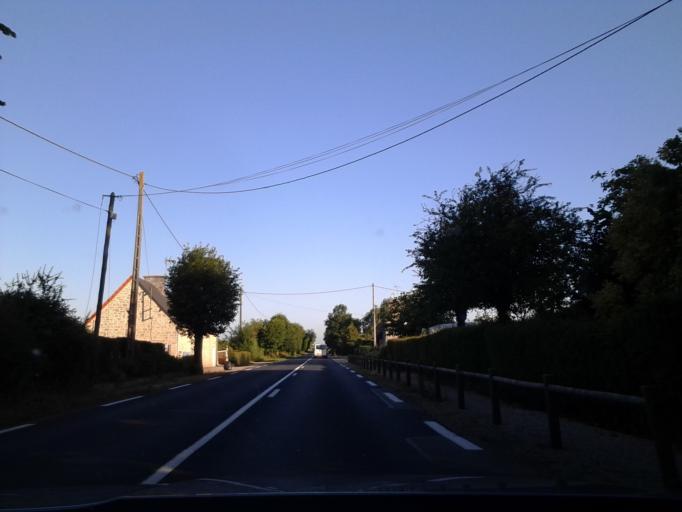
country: FR
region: Lower Normandy
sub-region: Departement de la Manche
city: Valognes
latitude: 49.5161
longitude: -1.4880
